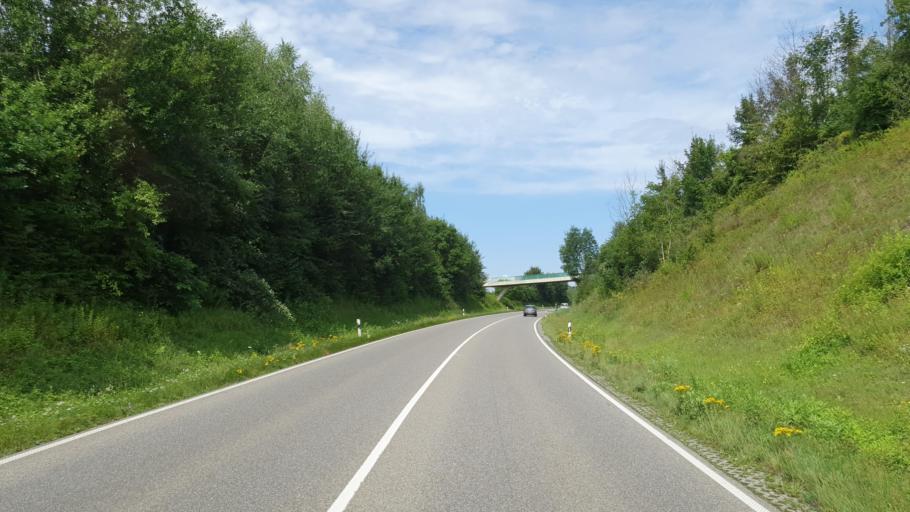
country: DE
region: Bavaria
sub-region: Swabia
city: Nonnenhorn
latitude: 47.5961
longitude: 9.6334
